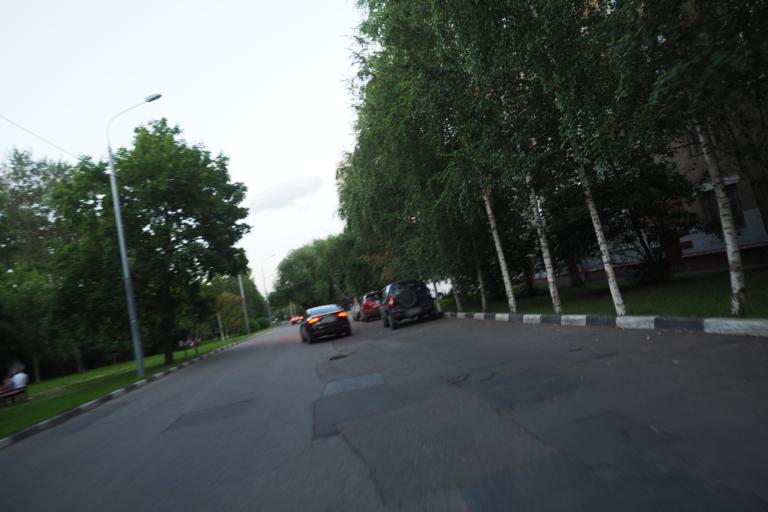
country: RU
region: Moscow
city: Kotlovka
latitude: 55.6804
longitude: 37.5996
